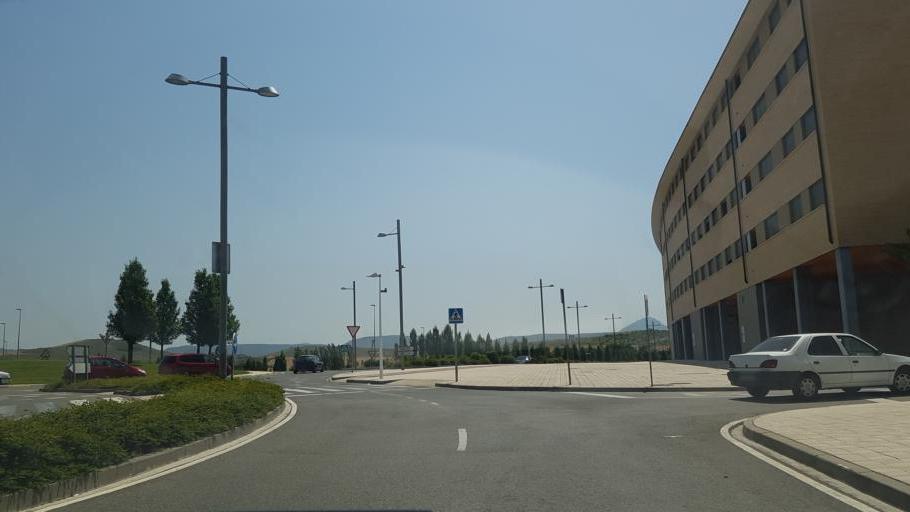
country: ES
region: Navarre
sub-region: Provincia de Navarra
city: Burlata
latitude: 42.7930
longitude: -1.6147
